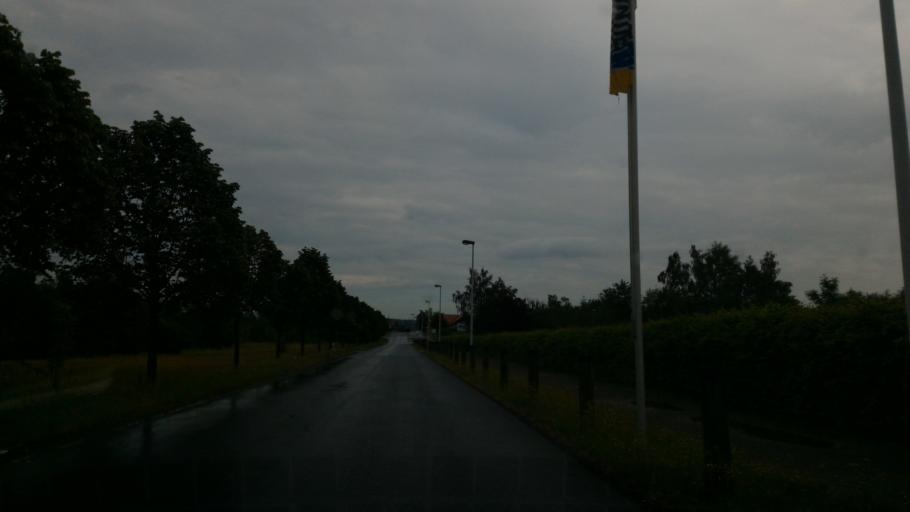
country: DE
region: Saxony
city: Olbersdorf
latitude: 50.8965
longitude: 14.7697
